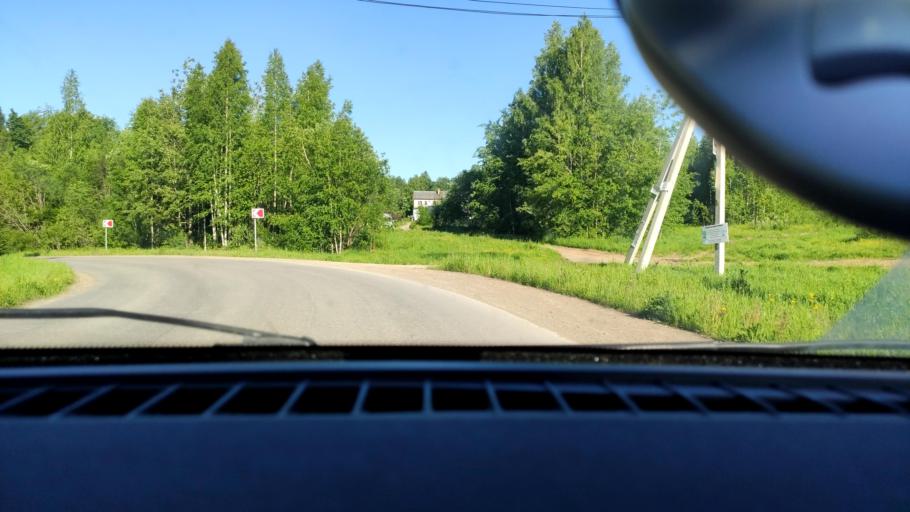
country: RU
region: Perm
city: Polazna
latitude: 58.2103
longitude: 56.5237
